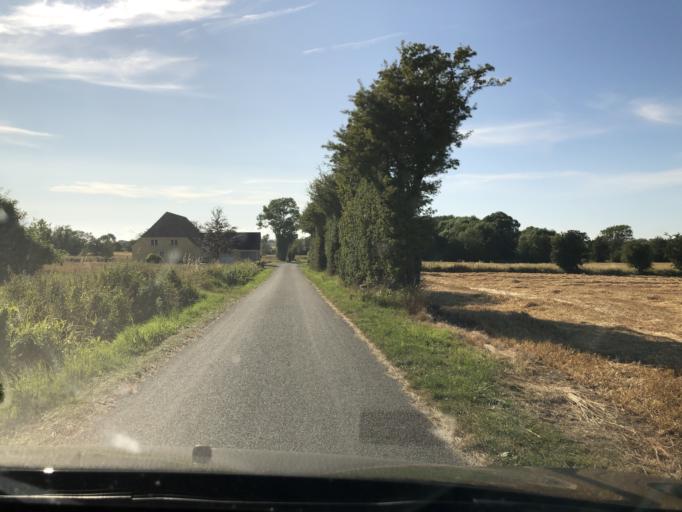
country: DK
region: South Denmark
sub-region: AEro Kommune
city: AEroskobing
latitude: 54.8540
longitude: 10.3691
